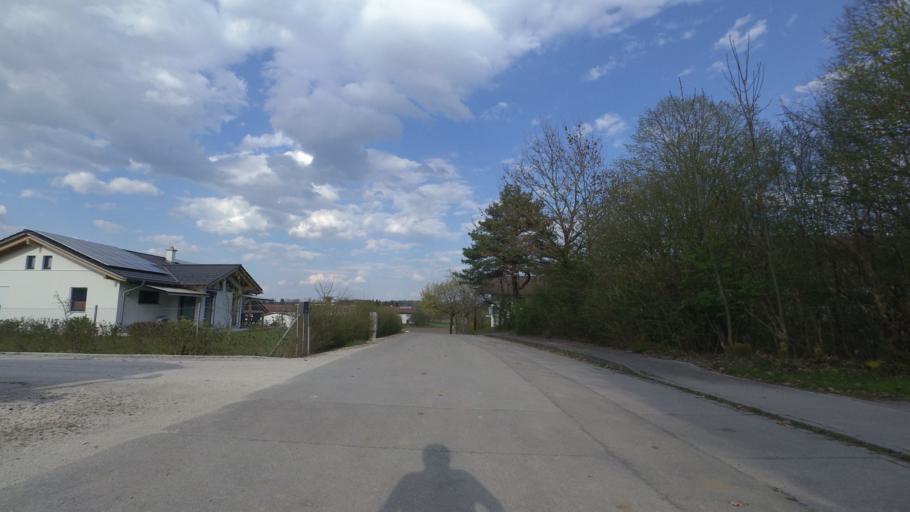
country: DE
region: Bavaria
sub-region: Upper Bavaria
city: Seeon-Seebruck
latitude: 47.9378
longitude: 12.4773
